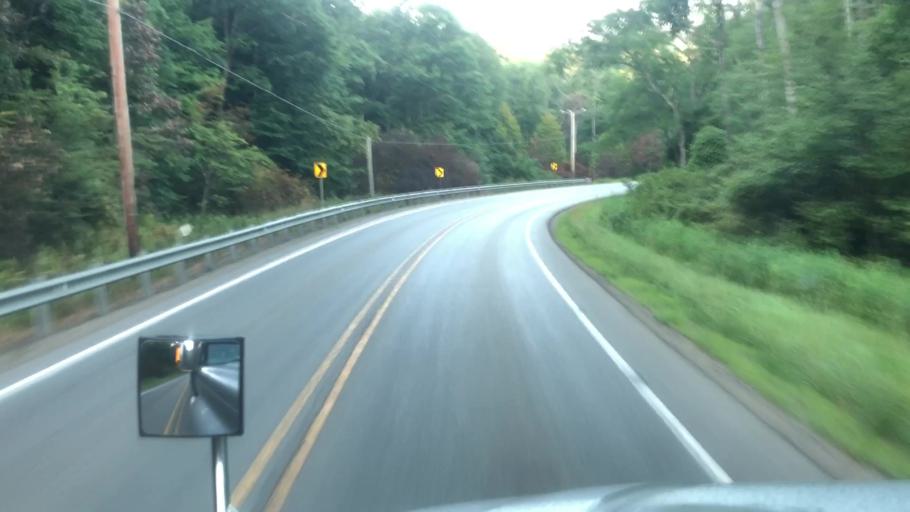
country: US
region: Pennsylvania
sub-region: Venango County
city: Hasson Heights
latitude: 41.4811
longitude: -79.6584
